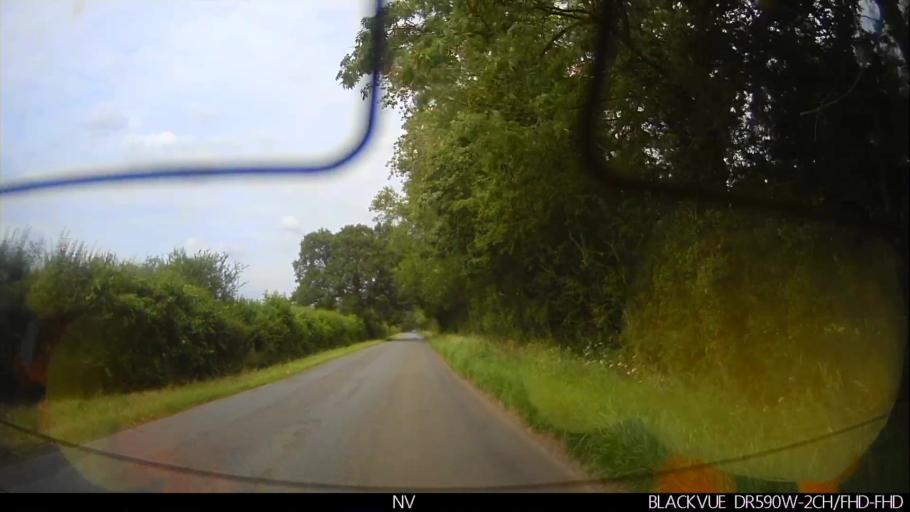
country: GB
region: England
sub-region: North Yorkshire
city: Strensall
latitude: 54.0393
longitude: -1.0177
